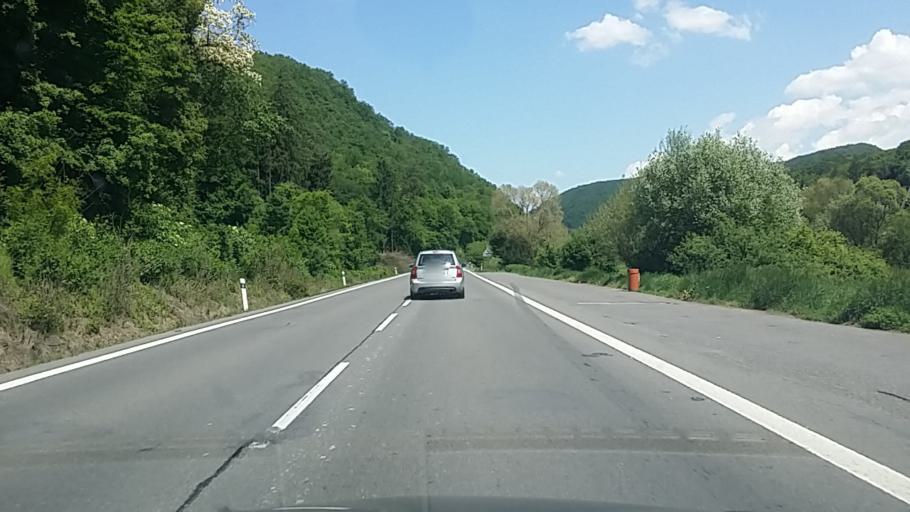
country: SK
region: Banskobystricky
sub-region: Okres Banska Bystrica
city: Zvolen
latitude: 48.5265
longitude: 19.1081
